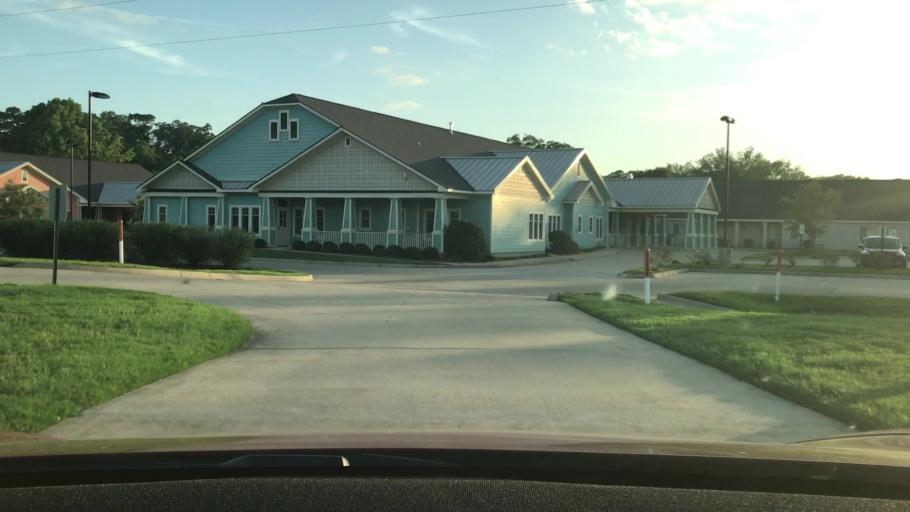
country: US
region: Louisiana
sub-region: Bossier Parish
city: Bossier City
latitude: 32.3981
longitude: -93.7189
